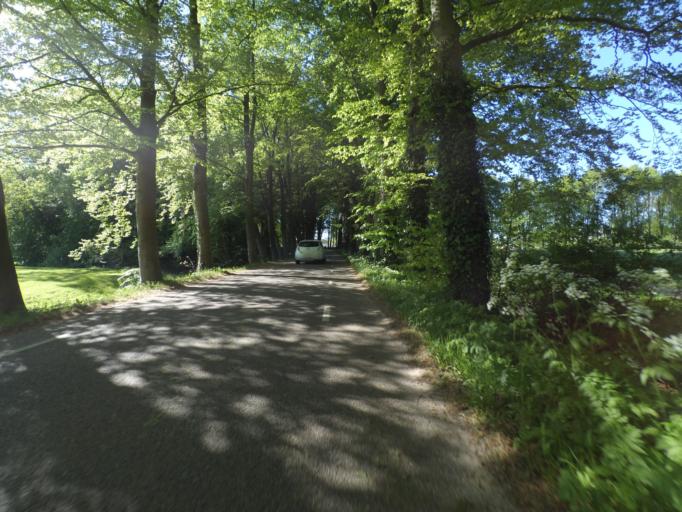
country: NL
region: Gelderland
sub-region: Gemeente Voorst
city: Wilp
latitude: 52.2003
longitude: 6.1257
